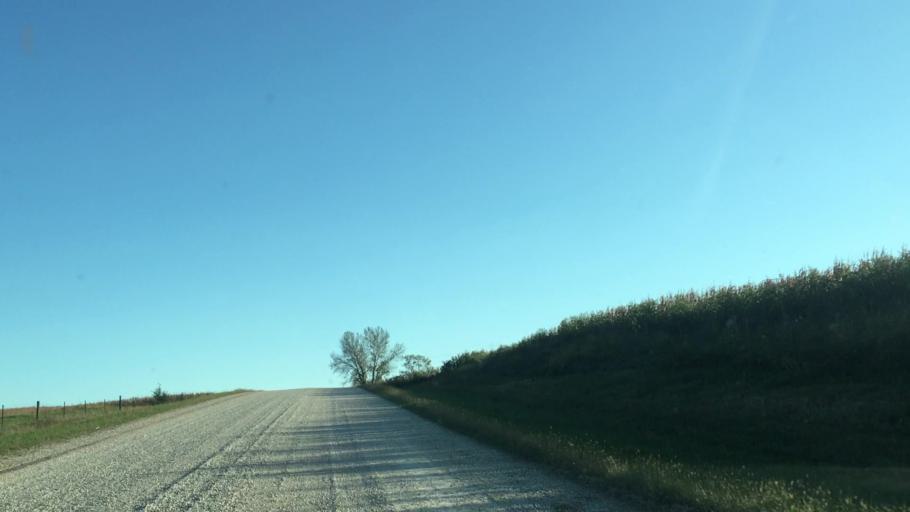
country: US
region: Minnesota
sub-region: Fillmore County
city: Preston
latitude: 43.8047
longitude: -92.0395
